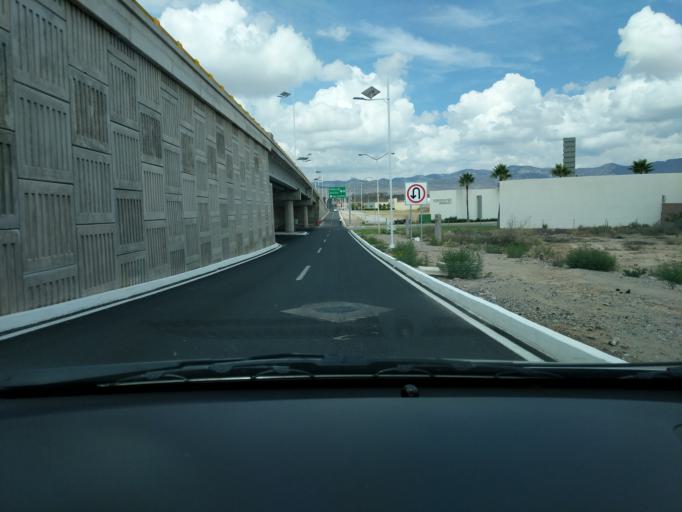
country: MX
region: San Luis Potosi
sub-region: Mexquitic de Carmona
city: Guadalupe Victoria
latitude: 22.1676
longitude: -101.0473
